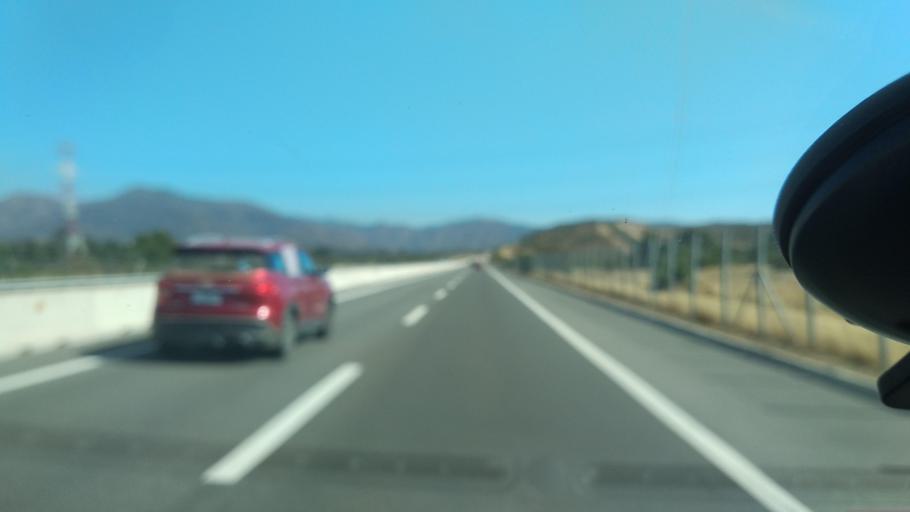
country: CL
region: Valparaiso
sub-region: Provincia de Marga Marga
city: Limache
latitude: -33.0198
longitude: -71.3195
